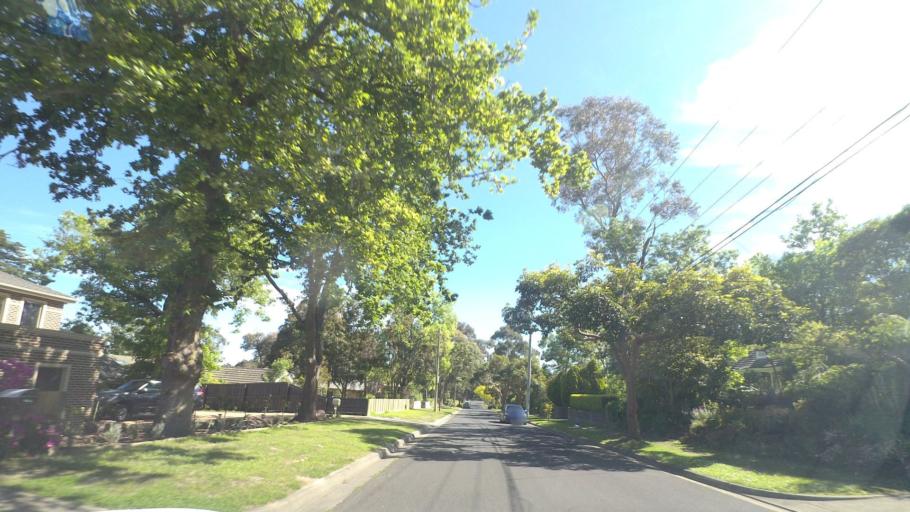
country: AU
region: Victoria
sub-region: Maroondah
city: Ringwood East
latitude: -37.8193
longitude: 145.2524
